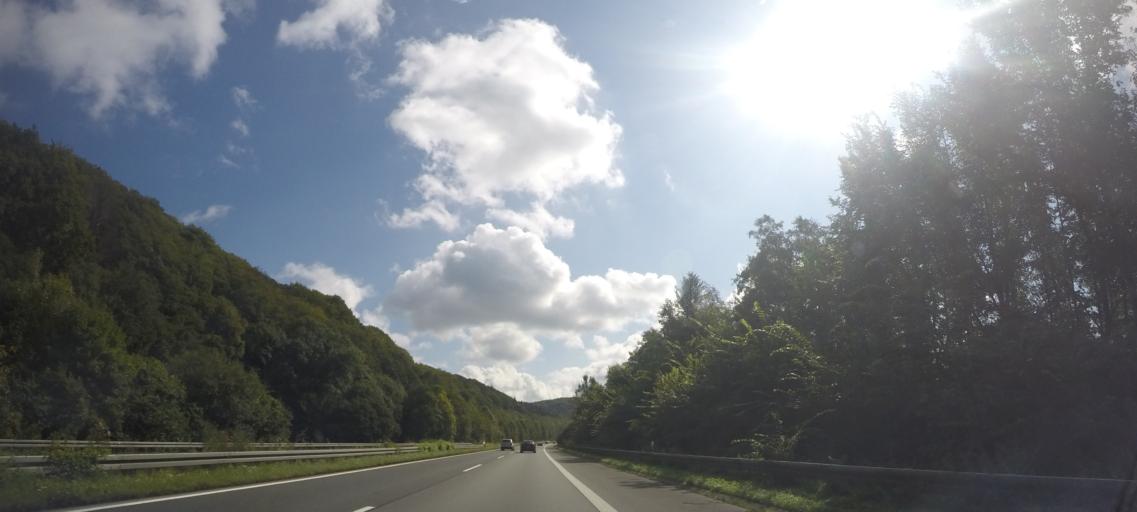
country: DE
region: North Rhine-Westphalia
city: Wickede
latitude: 51.4702
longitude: 7.9445
